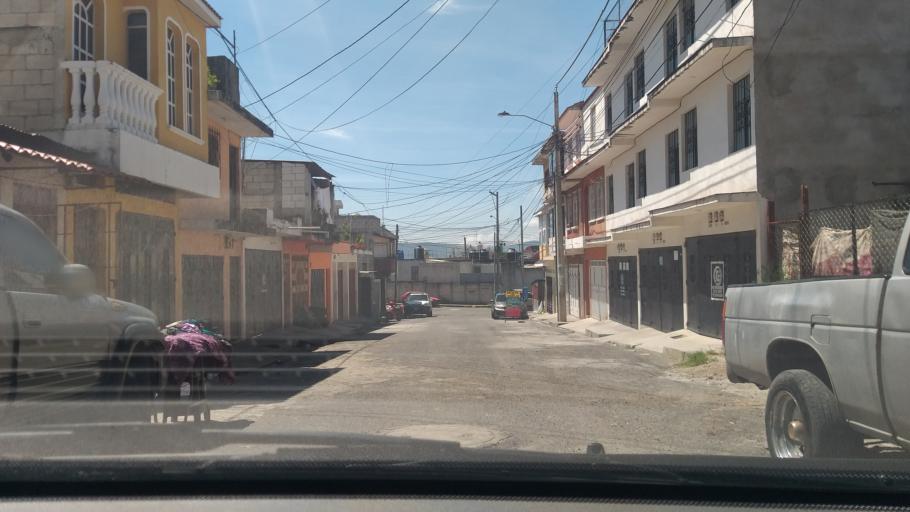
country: GT
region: Guatemala
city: Villa Nueva
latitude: 14.5386
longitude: -90.5537
